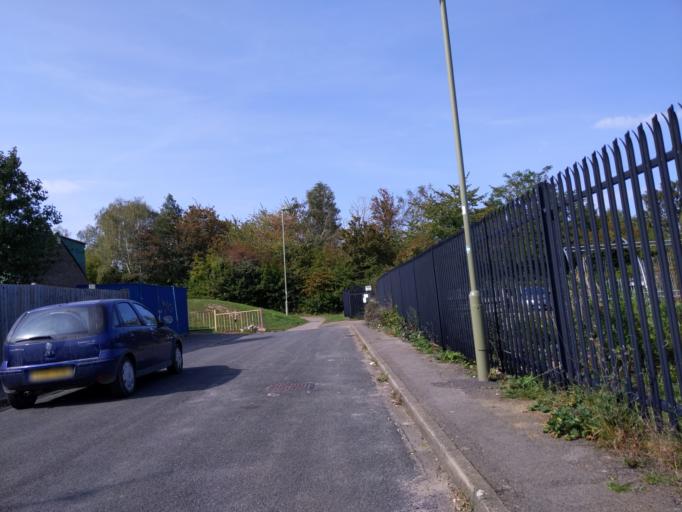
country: GB
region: England
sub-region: Oxfordshire
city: Cowley
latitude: 51.7223
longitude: -1.2288
